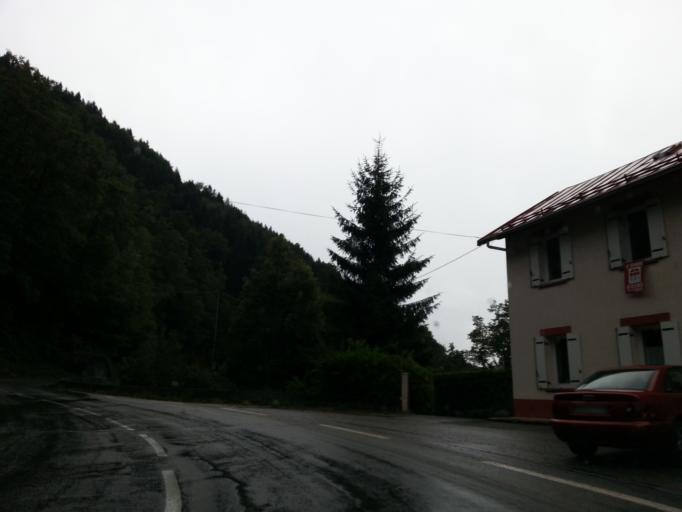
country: FR
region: Rhone-Alpes
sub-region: Departement de la Savoie
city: Marthod
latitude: 45.6976
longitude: 6.4267
